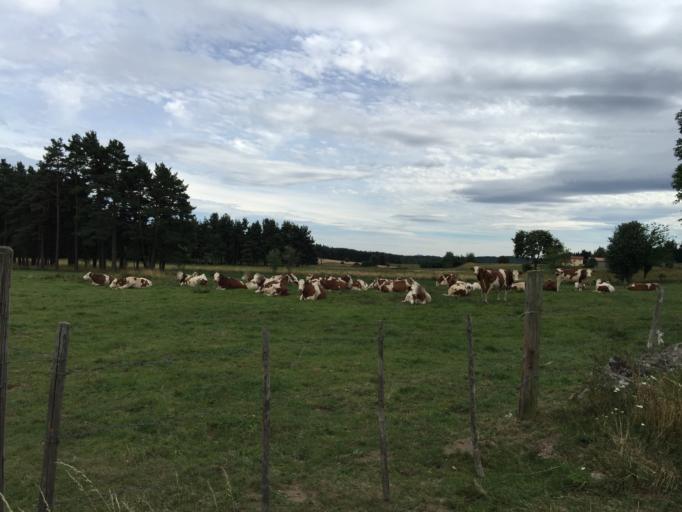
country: FR
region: Rhone-Alpes
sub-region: Departement de la Loire
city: Saint-Bonnet-le-Chateau
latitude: 45.3818
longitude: 4.0461
